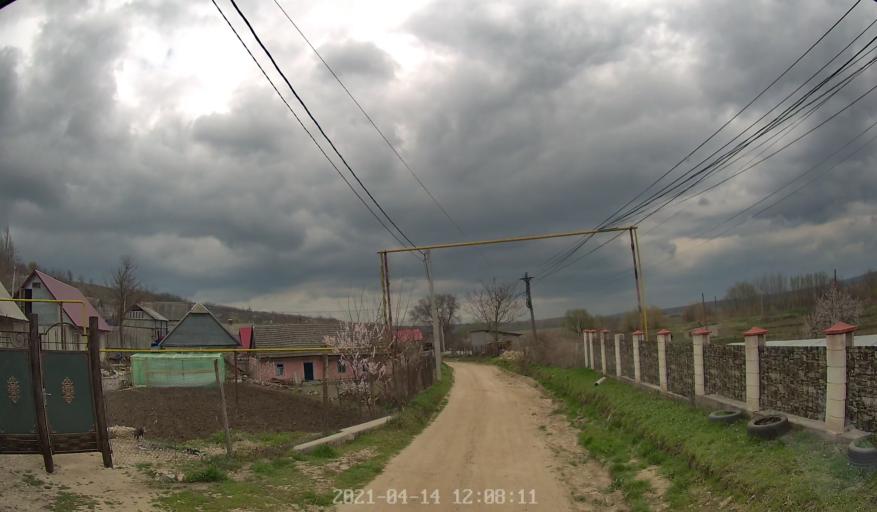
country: MD
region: Criuleni
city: Criuleni
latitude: 47.1709
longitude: 29.2120
